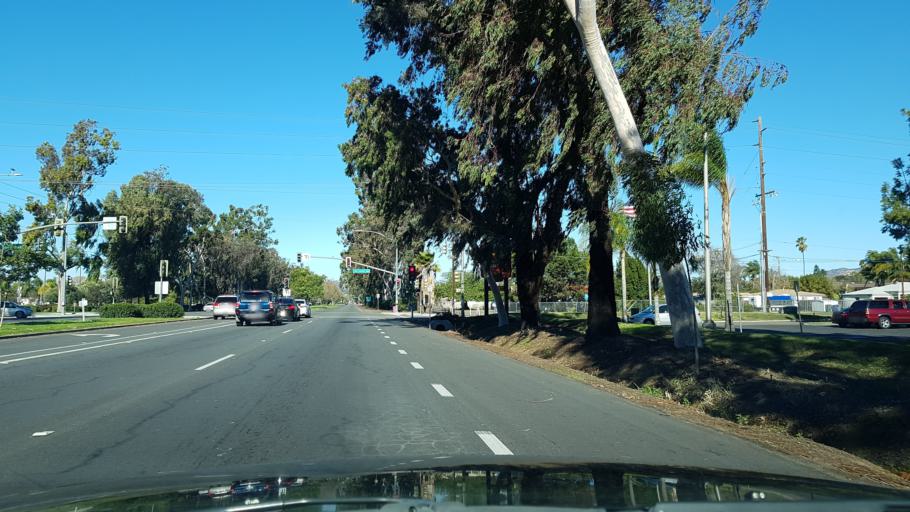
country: US
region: California
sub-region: San Diego County
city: Escondido
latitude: 33.1077
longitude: -117.0785
